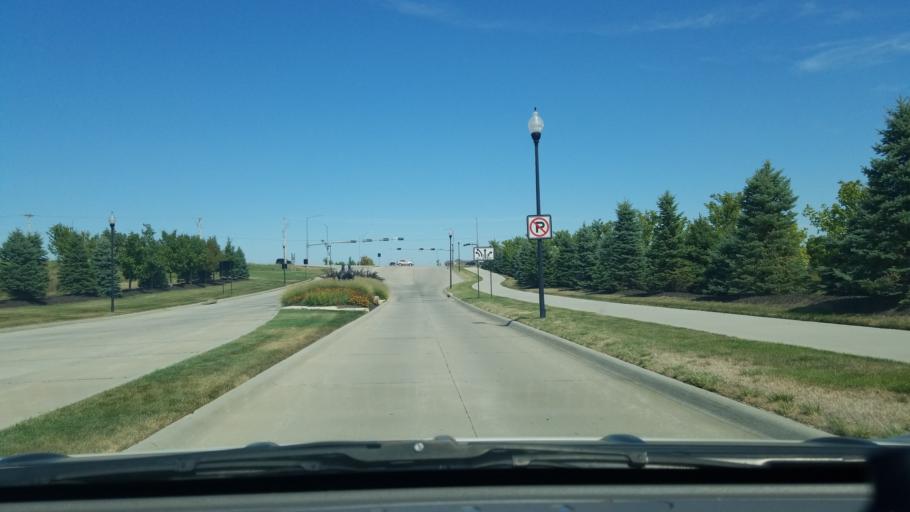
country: US
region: Nebraska
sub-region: Sarpy County
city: Papillion
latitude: 41.1461
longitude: -96.1009
